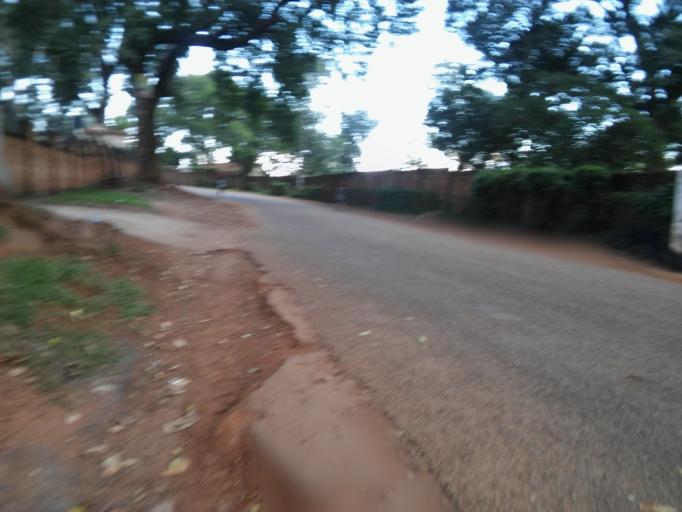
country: UG
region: Eastern Region
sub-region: Mbale District
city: Mbale
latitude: 1.0655
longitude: 34.1980
